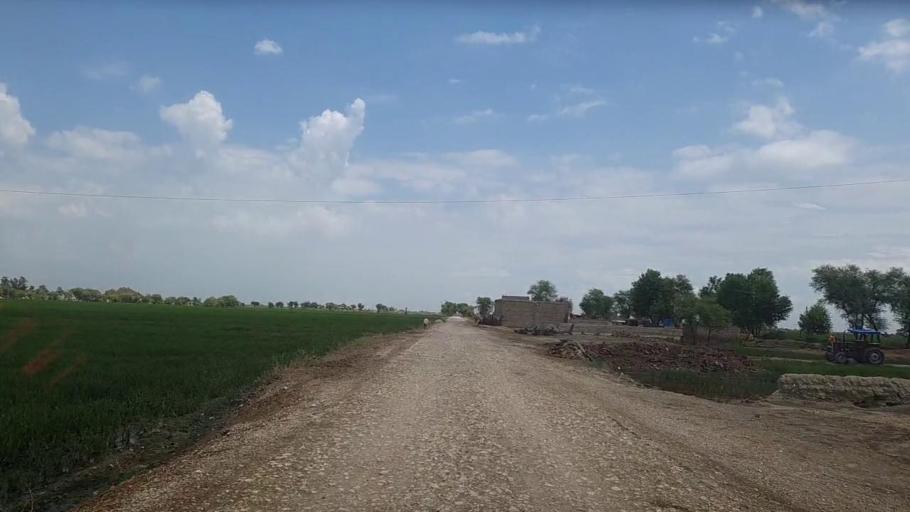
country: PK
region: Sindh
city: Kandhkot
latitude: 28.3422
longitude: 69.2145
